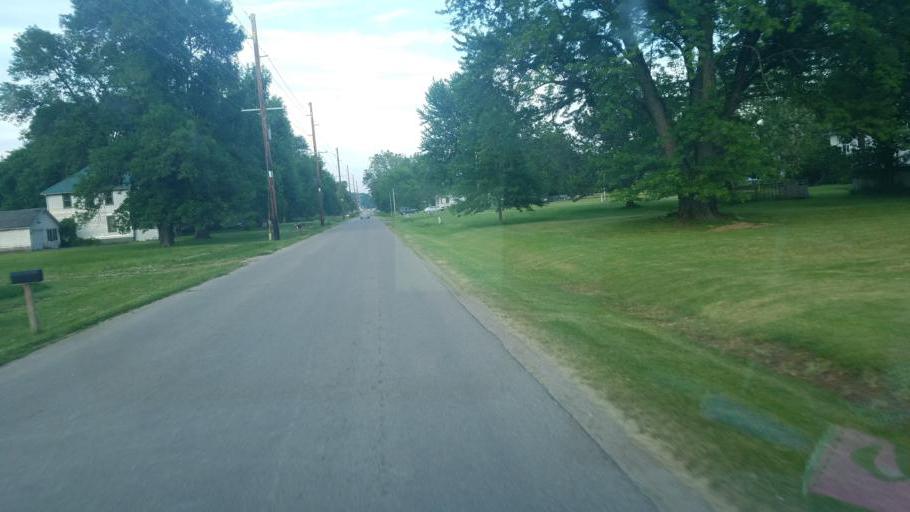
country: US
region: Iowa
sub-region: Benton County
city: Belle Plaine
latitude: 41.9203
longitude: -92.3929
